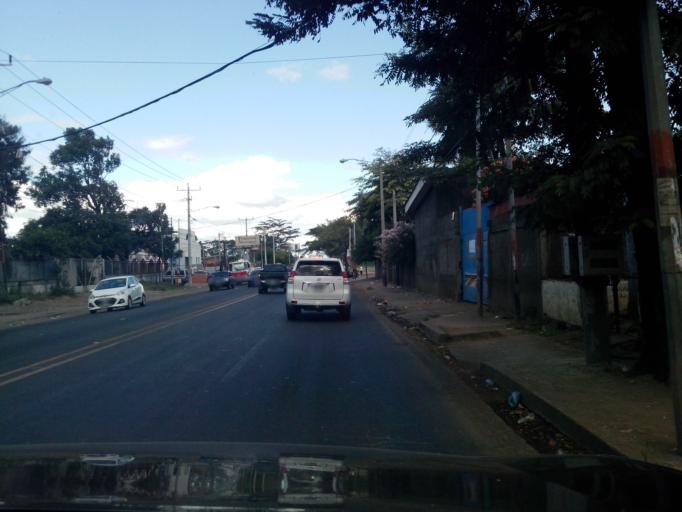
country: NI
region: Managua
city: Ciudad Sandino
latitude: 12.1246
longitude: -86.3126
